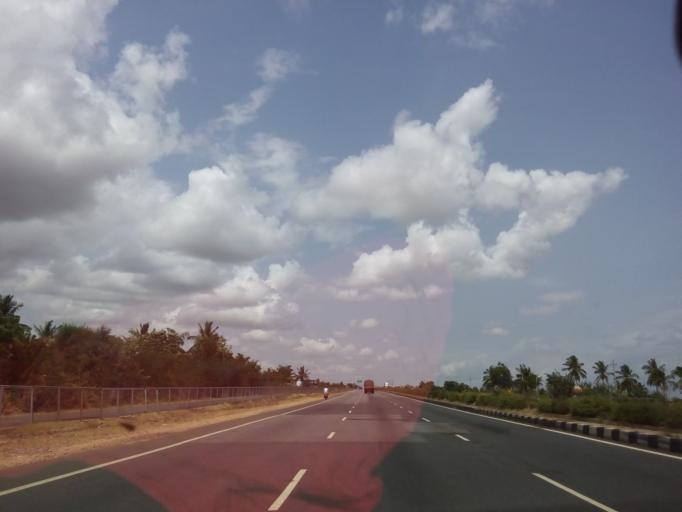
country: IN
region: Karnataka
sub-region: Tumkur
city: Sira
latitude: 13.7657
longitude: 76.8562
